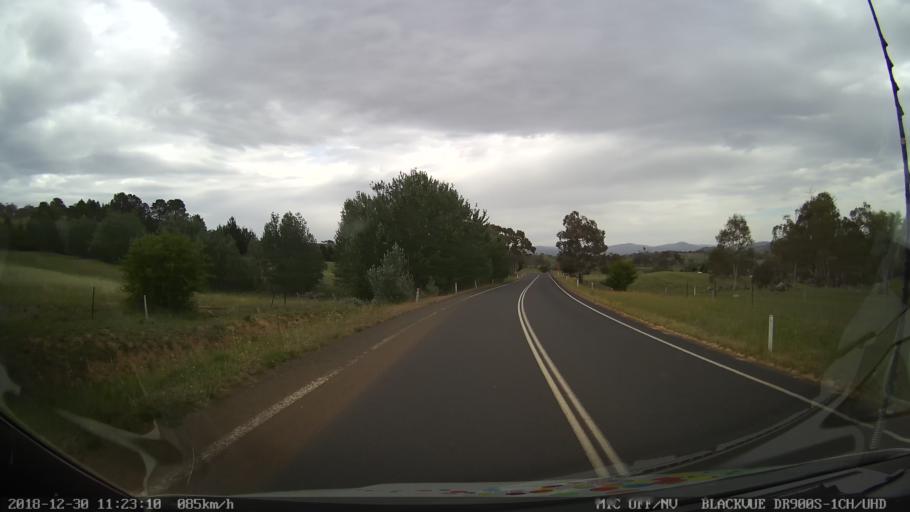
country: AU
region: New South Wales
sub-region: Snowy River
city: Jindabyne
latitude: -36.4924
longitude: 148.6658
